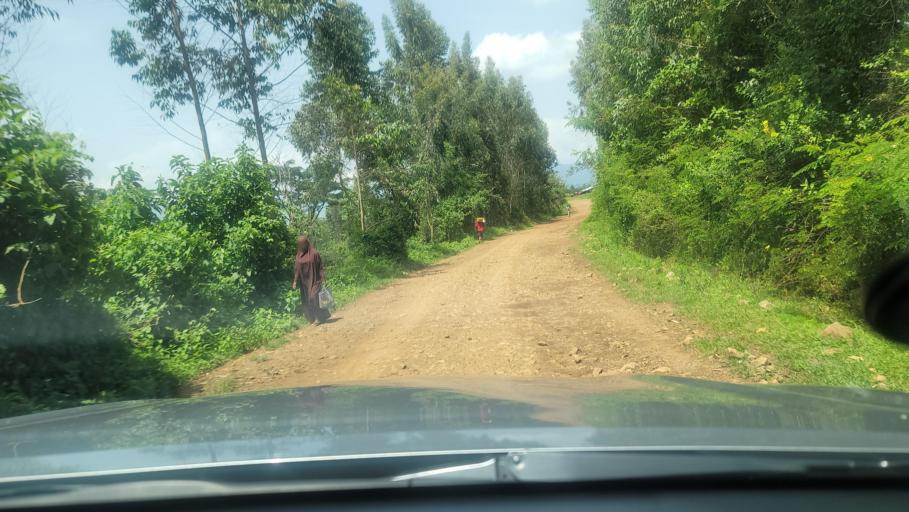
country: ET
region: Oromiya
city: Agaro
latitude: 7.8002
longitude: 36.4175
